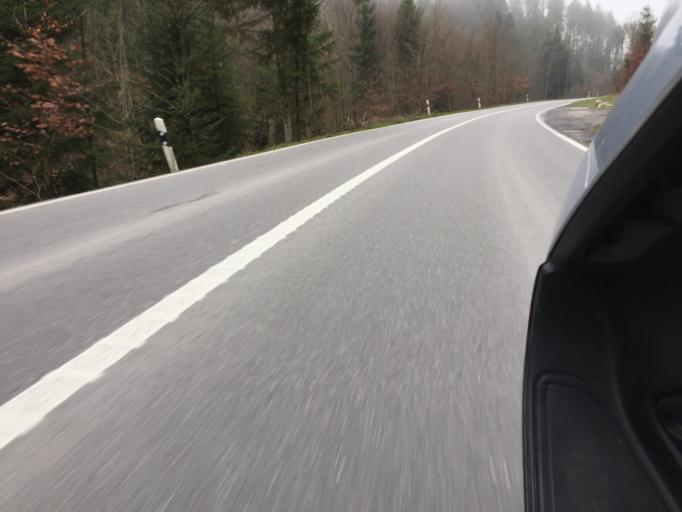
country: CH
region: Solothurn
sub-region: Bezirk Bucheggberg
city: Messen
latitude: 47.0760
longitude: 7.4089
